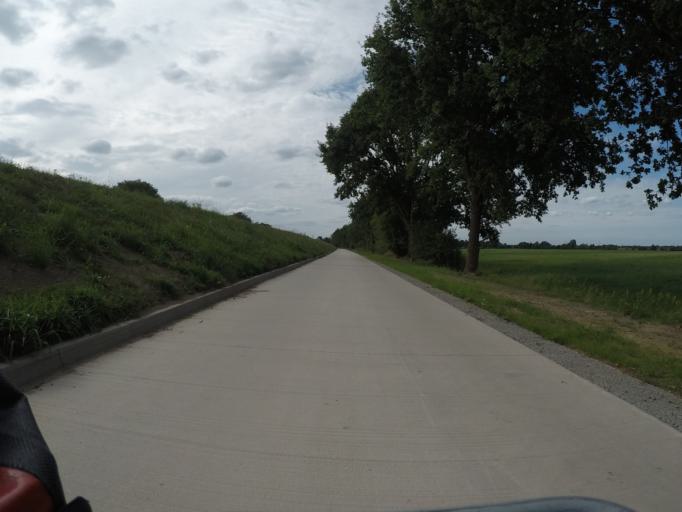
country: DE
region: Lower Saxony
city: Handorf
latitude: 53.3524
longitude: 10.3720
